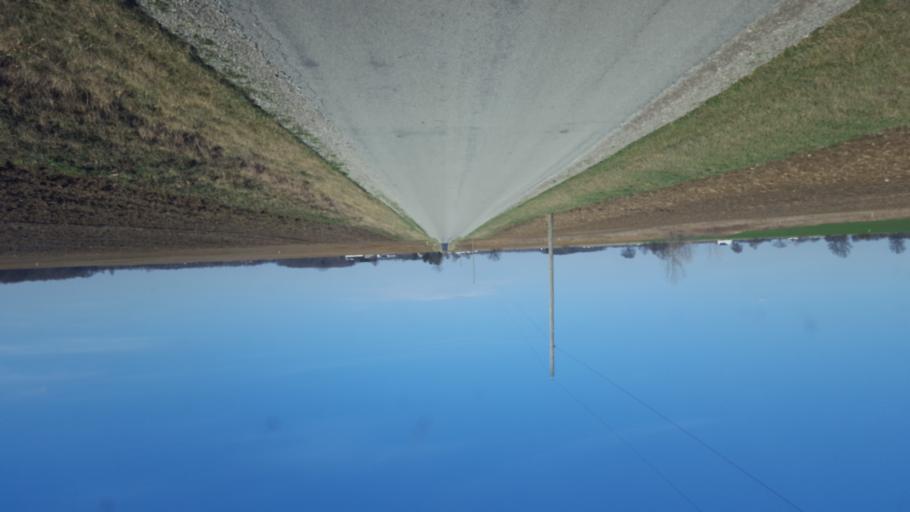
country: US
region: Ohio
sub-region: Crawford County
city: Bucyrus
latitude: 40.7043
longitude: -82.9370
